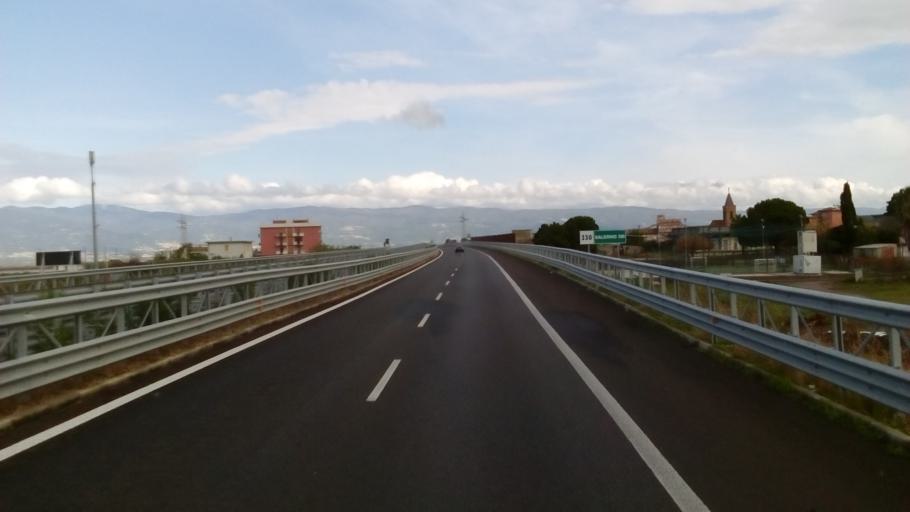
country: IT
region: Calabria
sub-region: Provincia di Catanzaro
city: Acconia
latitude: 38.8372
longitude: 16.2599
